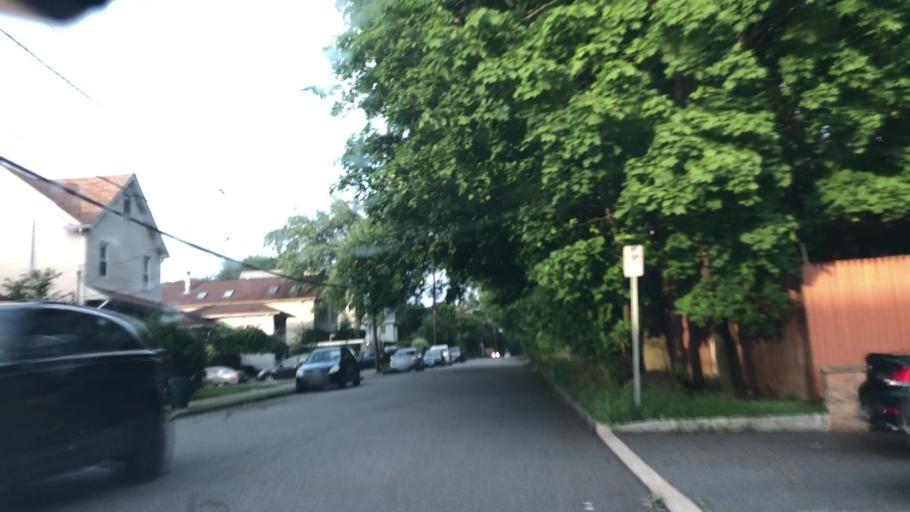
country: US
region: New Jersey
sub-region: Passaic County
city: Little Falls
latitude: 40.8784
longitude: -74.2093
